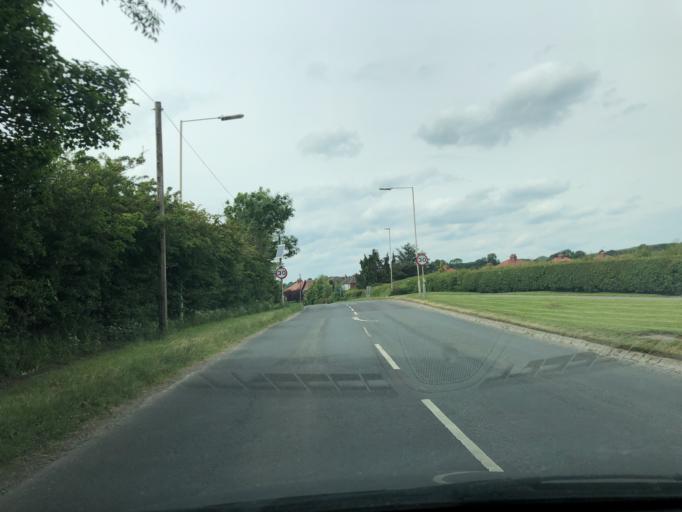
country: GB
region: England
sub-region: North Yorkshire
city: Pickering
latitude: 54.2391
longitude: -0.7608
